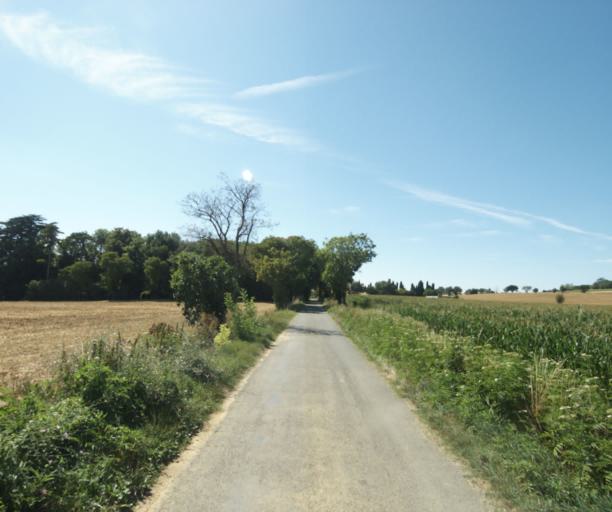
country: FR
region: Midi-Pyrenees
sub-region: Departement de la Haute-Garonne
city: Saint-Felix-Lauragais
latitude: 43.5111
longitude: 1.9140
